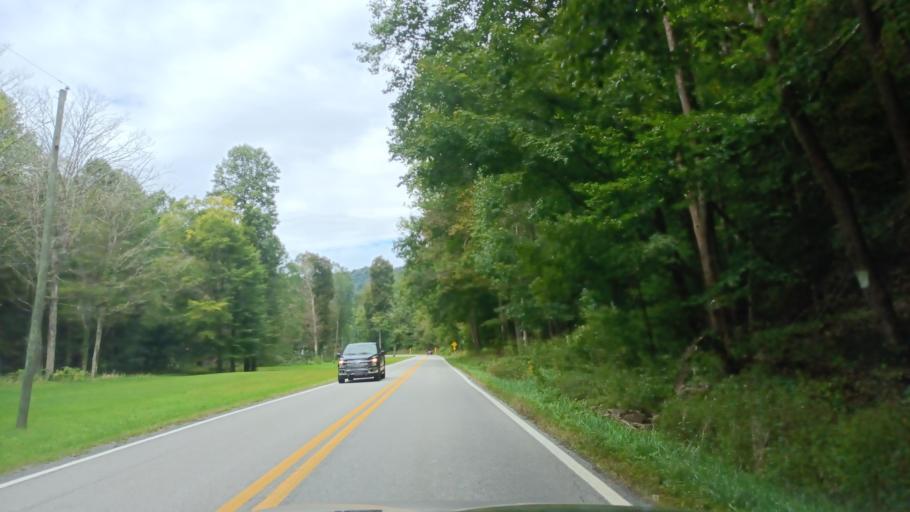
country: US
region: West Virginia
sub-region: Preston County
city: Kingwood
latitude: 39.3198
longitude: -79.7100
